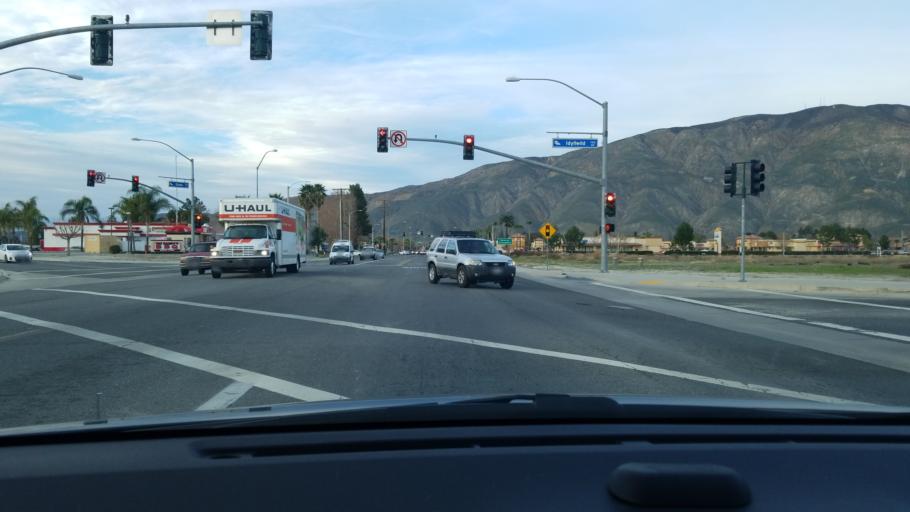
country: US
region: California
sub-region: Riverside County
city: San Jacinto
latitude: 33.7996
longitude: -116.9720
